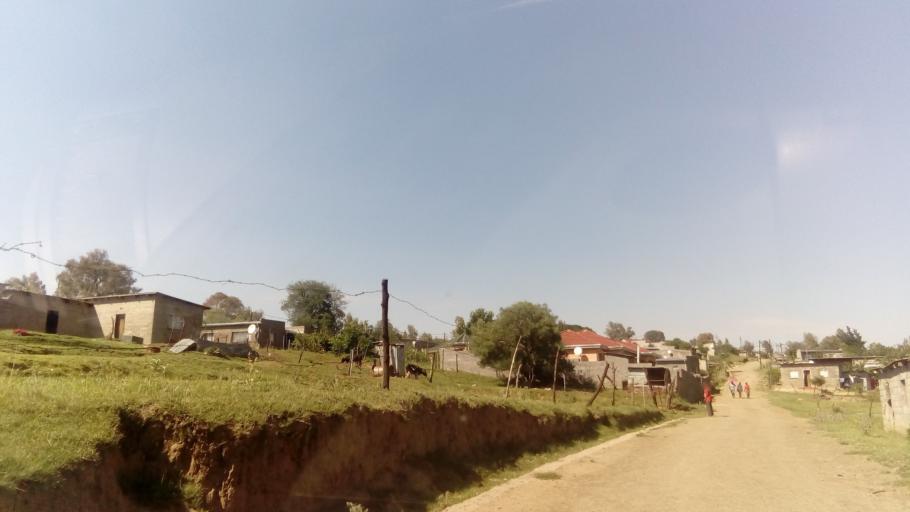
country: LS
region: Berea
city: Teyateyaneng
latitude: -29.1443
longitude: 27.7581
